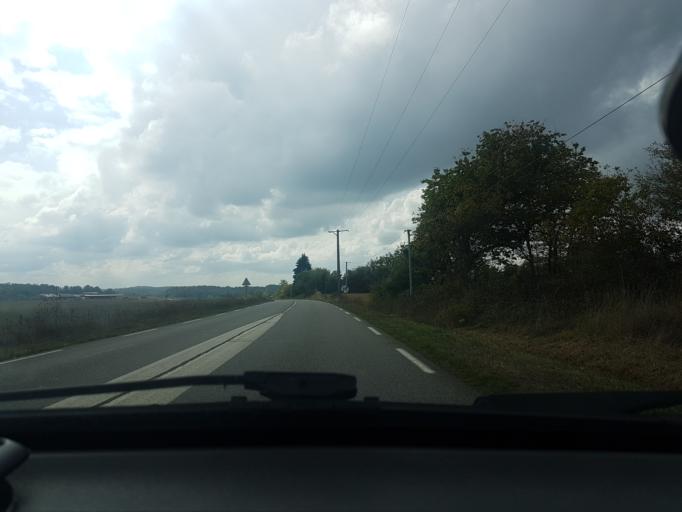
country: FR
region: Franche-Comte
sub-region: Departement de la Haute-Saone
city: Villersexel
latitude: 47.5478
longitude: 6.4385
